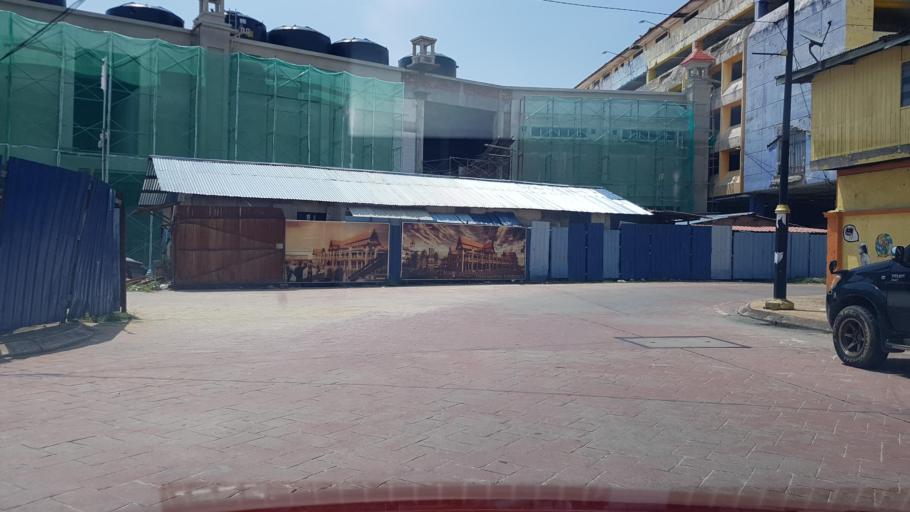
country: MY
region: Terengganu
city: Kuala Terengganu
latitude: 5.3354
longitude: 103.1347
